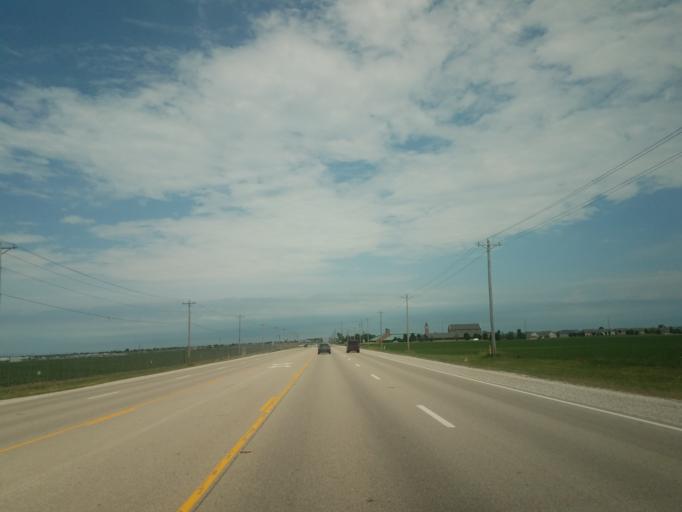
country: US
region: Illinois
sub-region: McLean County
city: Bloomington
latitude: 40.4836
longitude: -88.9024
